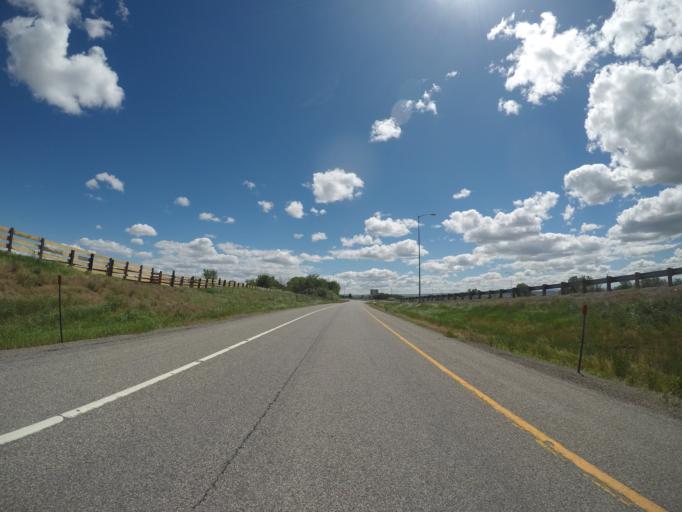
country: US
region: Montana
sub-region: Yellowstone County
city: Laurel
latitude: 45.6365
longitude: -108.9121
